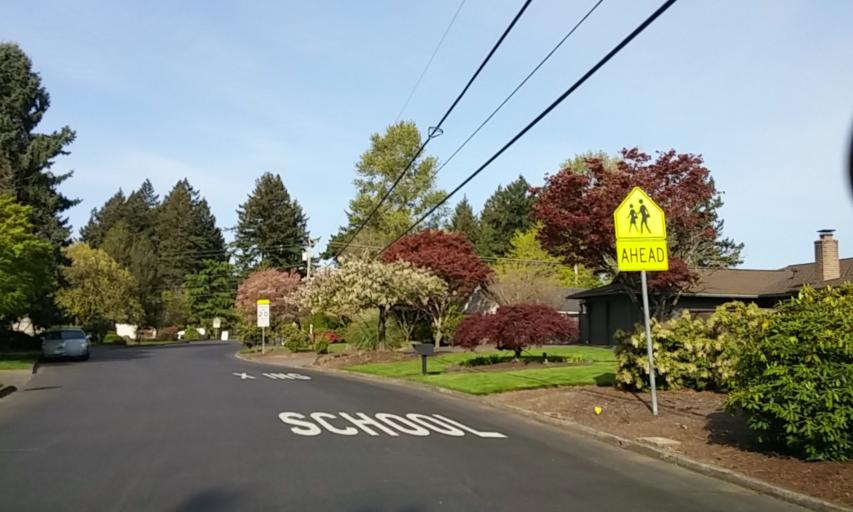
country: US
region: Oregon
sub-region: Washington County
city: West Slope
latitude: 45.5014
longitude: -122.7789
